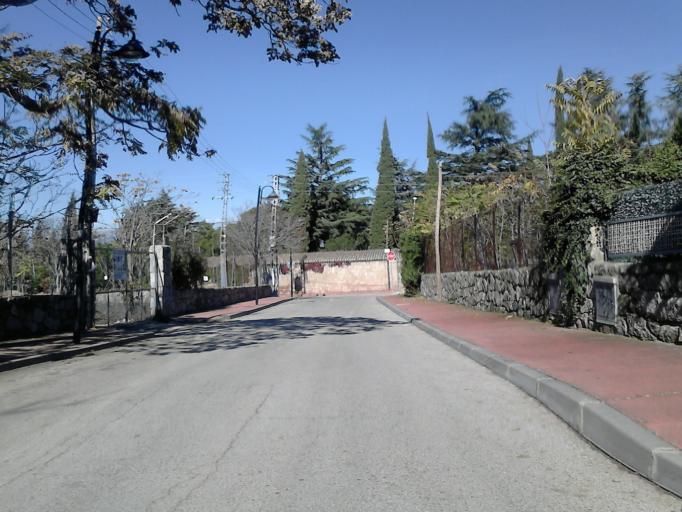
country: ES
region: Madrid
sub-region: Provincia de Madrid
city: Galapagar
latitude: 40.5734
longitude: -3.9957
